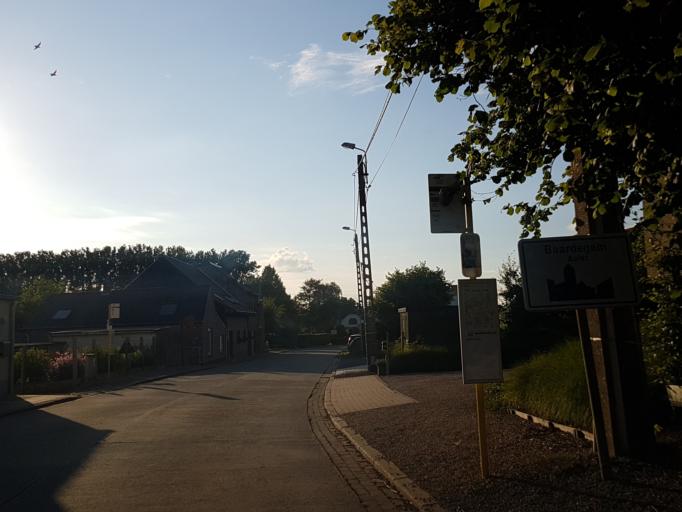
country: BE
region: Flanders
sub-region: Provincie Vlaams-Brabant
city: Opwijk
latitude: 50.9470
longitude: 4.1400
